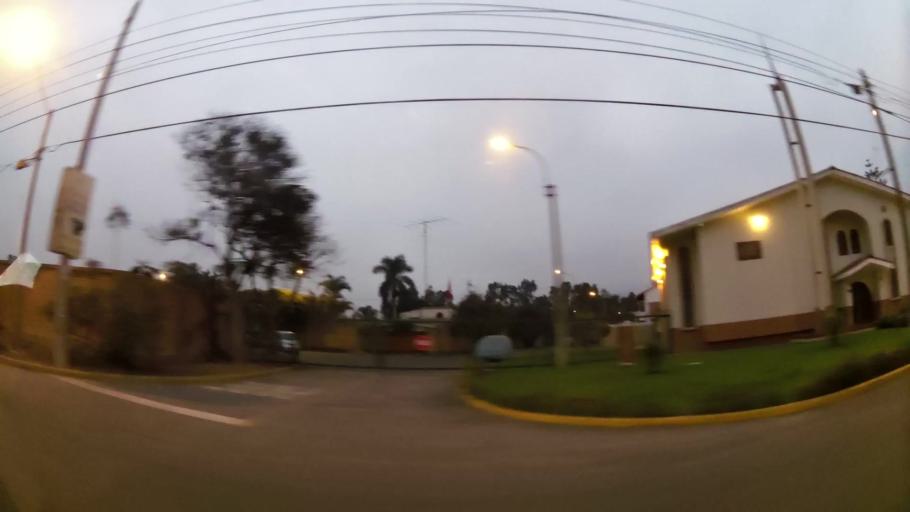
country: PE
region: Lima
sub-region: Lima
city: La Molina
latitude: -12.0879
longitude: -76.9501
